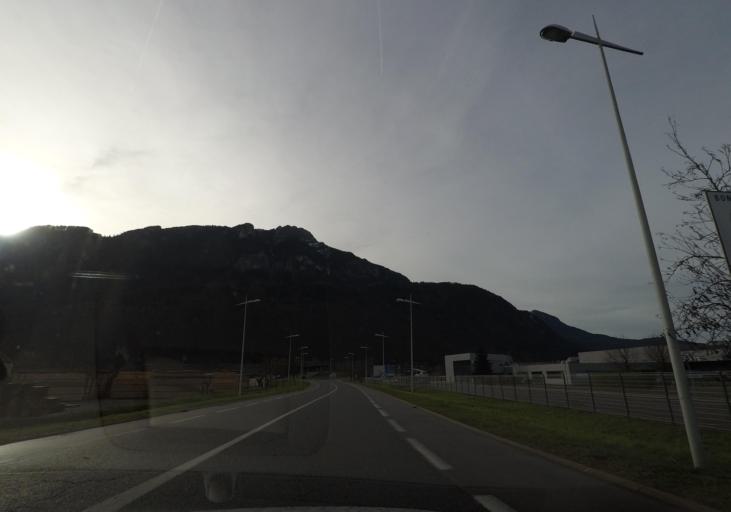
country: FR
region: Rhone-Alpes
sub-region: Departement de la Haute-Savoie
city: Ayse
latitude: 46.0730
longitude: 6.4266
